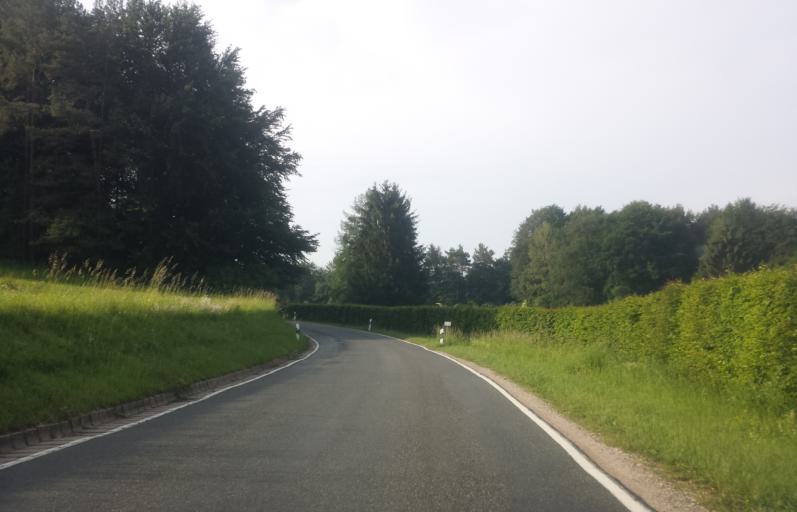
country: DE
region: Bavaria
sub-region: Upper Franconia
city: Ebermannstadt
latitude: 49.7751
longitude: 11.2512
